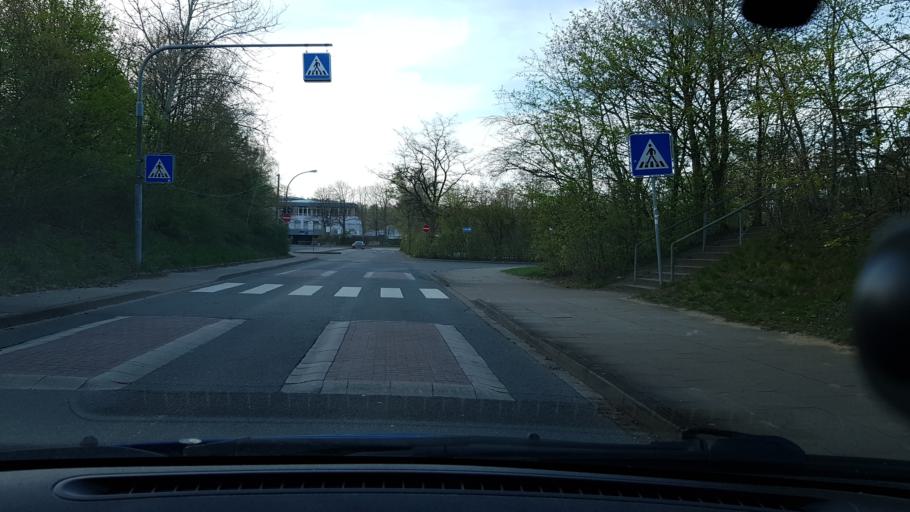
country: DE
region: Lower Saxony
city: Buchholz in der Nordheide
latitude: 53.3225
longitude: 9.8426
